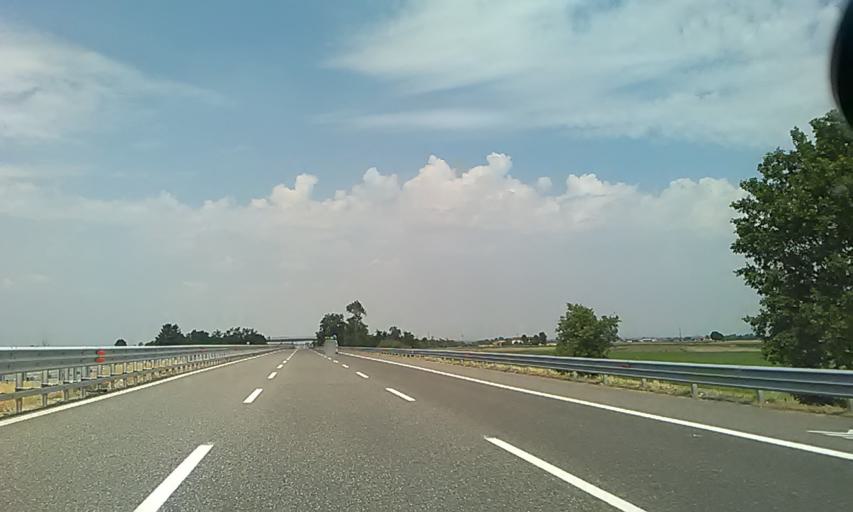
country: IT
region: Piedmont
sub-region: Provincia di Alessandria
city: Castelspina
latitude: 44.7833
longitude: 8.6203
